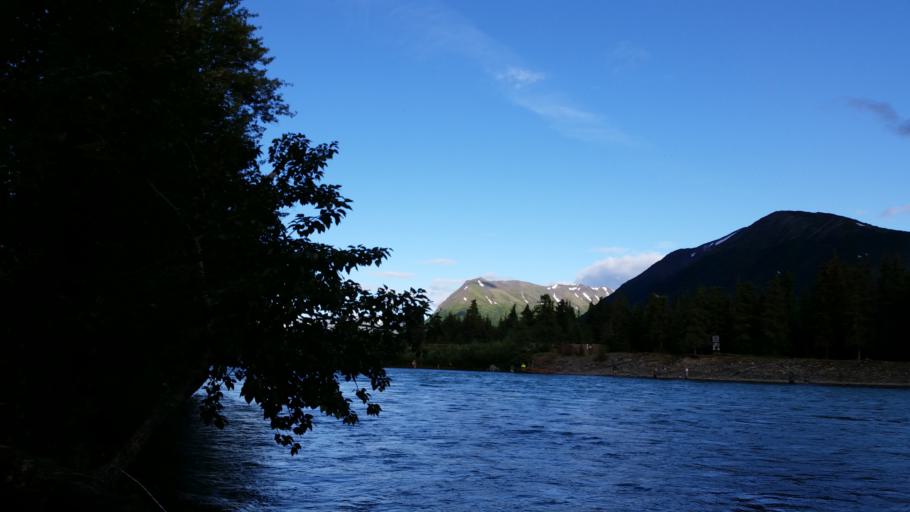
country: US
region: Alaska
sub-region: Kenai Peninsula Borough
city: Seward
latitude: 60.4846
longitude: -150.0074
